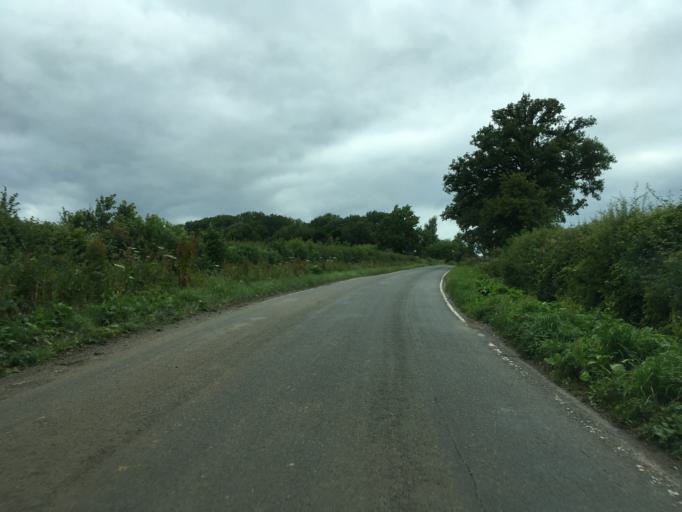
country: GB
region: England
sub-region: Gloucestershire
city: Dursley
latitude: 51.7825
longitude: -2.3925
